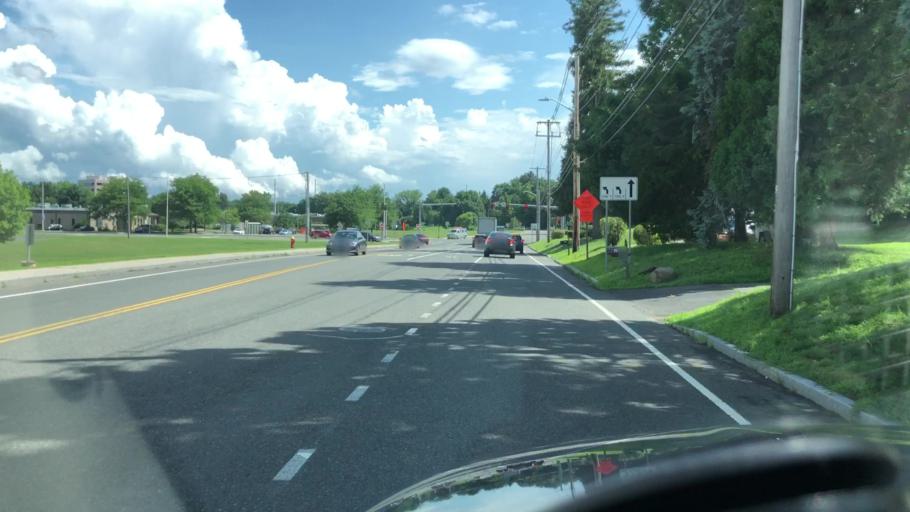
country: US
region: Massachusetts
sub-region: Hampden County
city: Holyoke
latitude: 42.1754
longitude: -72.6485
